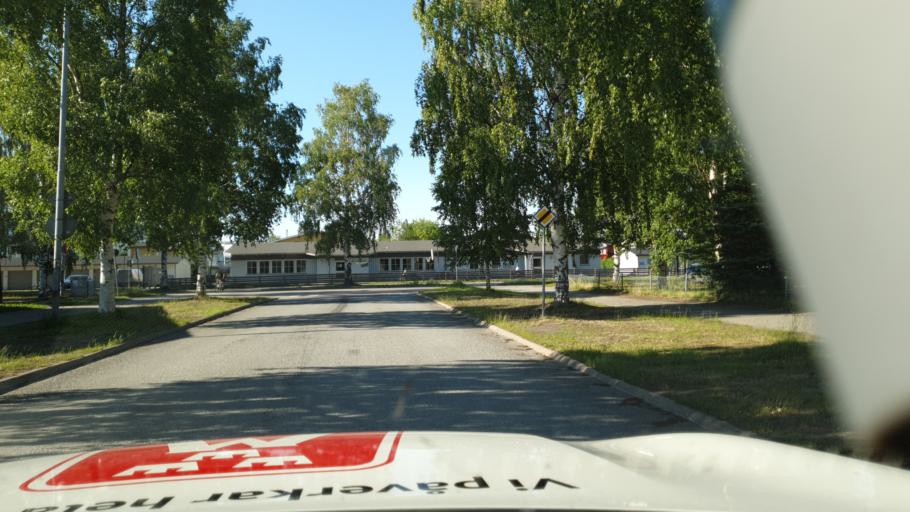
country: SE
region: Vaesterbotten
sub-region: Umea Kommun
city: Roback
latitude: 63.8177
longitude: 20.2131
